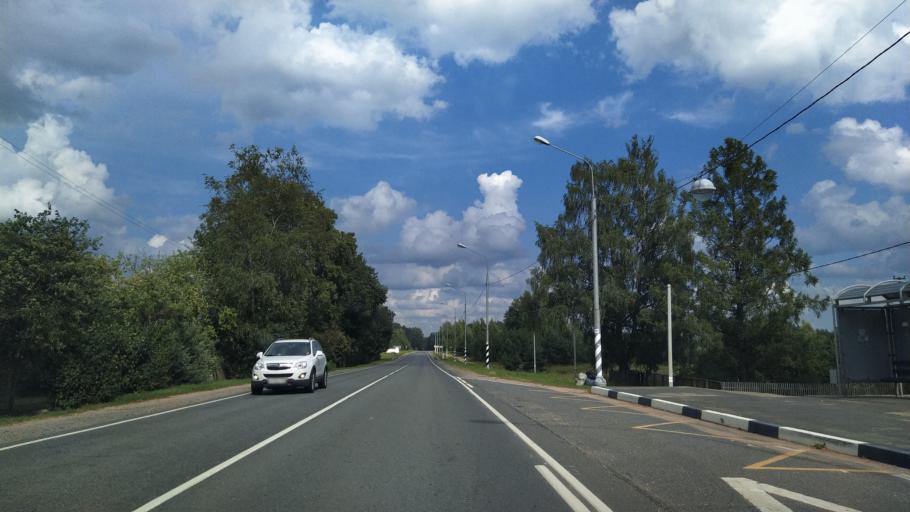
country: RU
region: Novgorod
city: Sol'tsy
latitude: 58.1021
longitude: 30.2026
